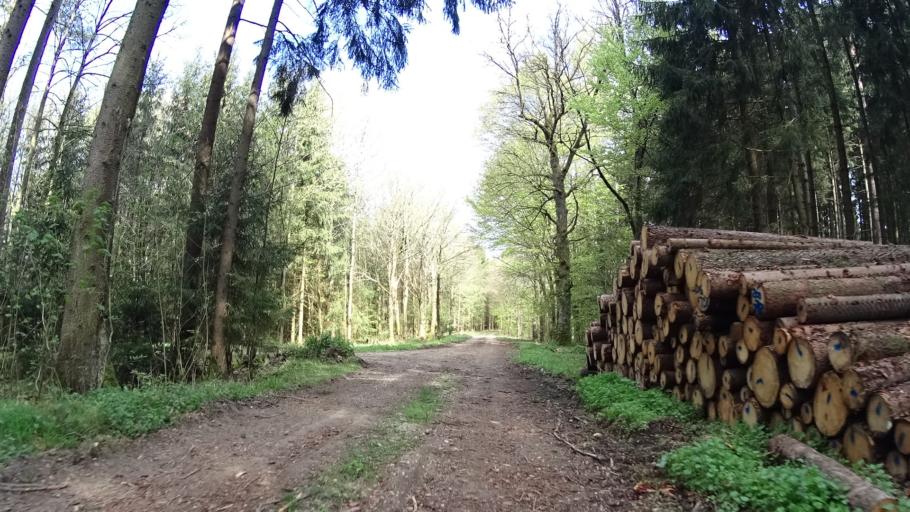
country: DE
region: Bavaria
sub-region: Upper Bavaria
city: Wettstetten
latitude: 48.8512
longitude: 11.4059
